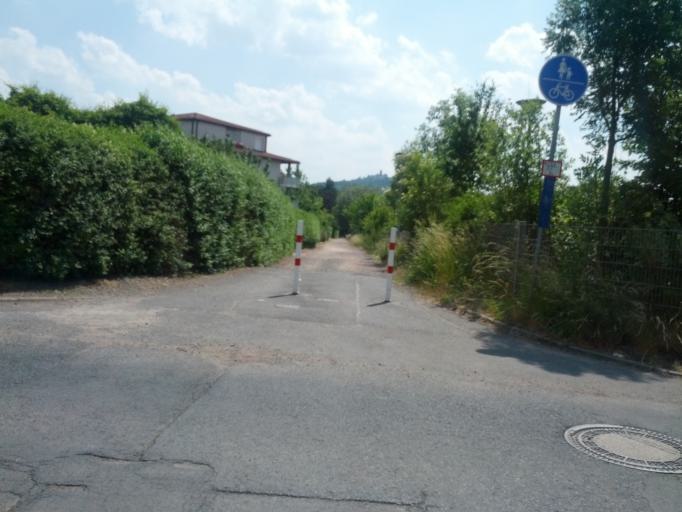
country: DE
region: Thuringia
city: Eisenach
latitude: 50.9896
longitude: 10.3182
